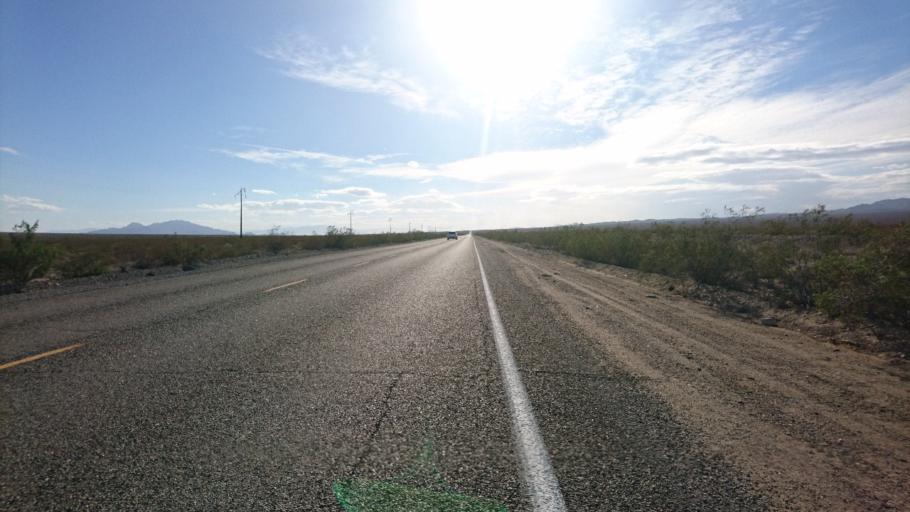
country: US
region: California
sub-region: San Bernardino County
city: Needles
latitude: 34.7007
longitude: -115.2977
